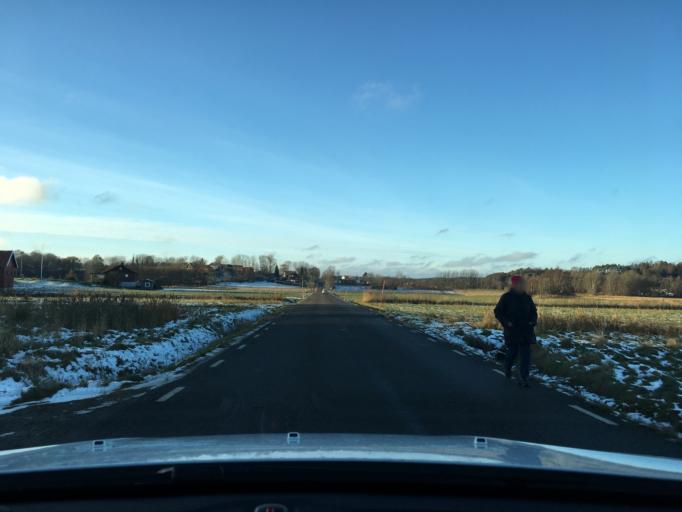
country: SE
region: Vaestra Goetaland
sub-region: Tjorns Kommun
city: Myggenas
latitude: 58.0472
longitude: 11.7225
